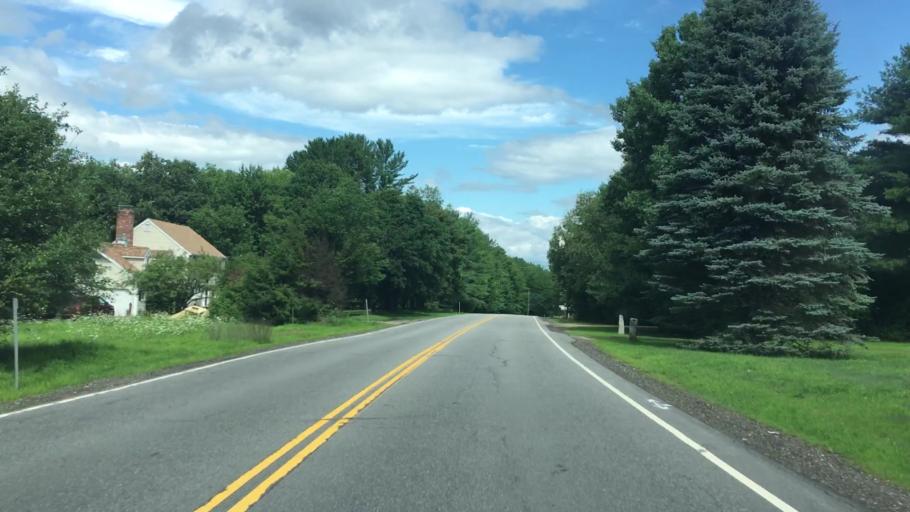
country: US
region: New Hampshire
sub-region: Belknap County
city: Meredith
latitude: 43.5859
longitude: -71.5168
